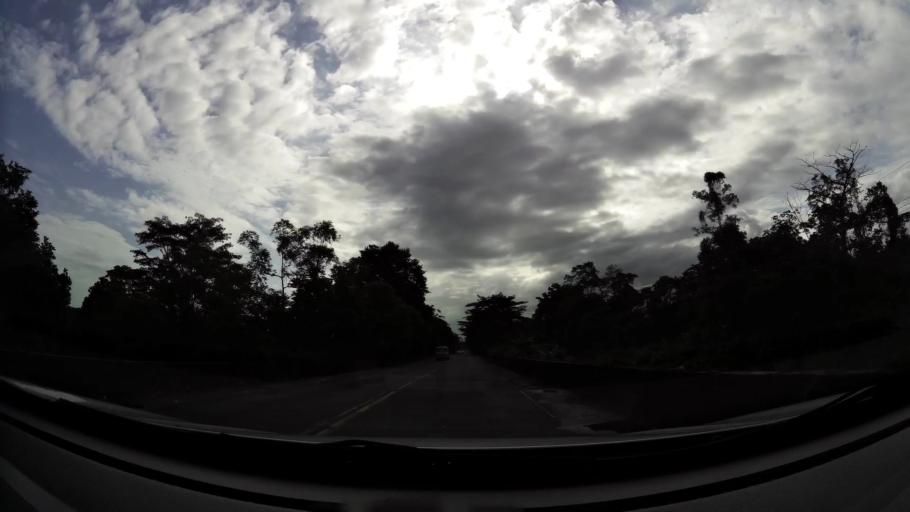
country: CR
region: Limon
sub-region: Canton de Guacimo
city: Guacimo
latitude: 10.2057
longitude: -83.6842
